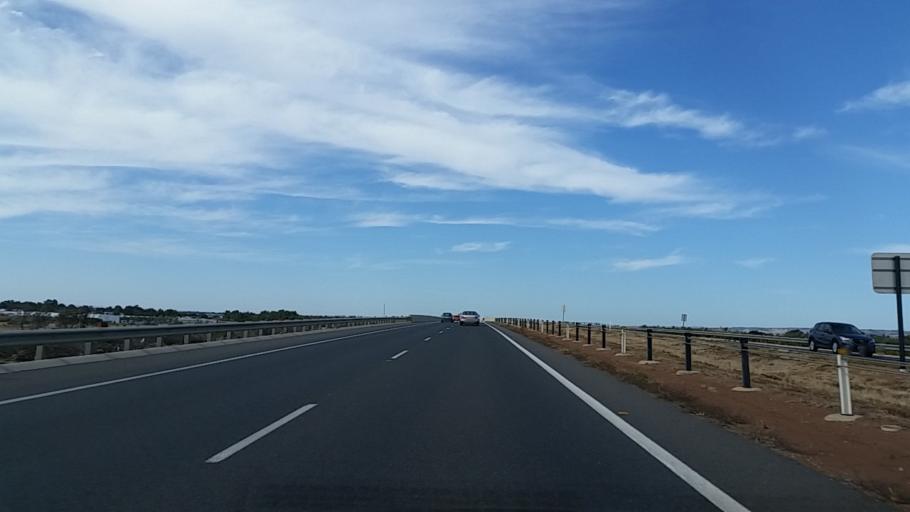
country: AU
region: South Australia
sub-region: Playford
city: Virginia
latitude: -34.6932
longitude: 138.5853
